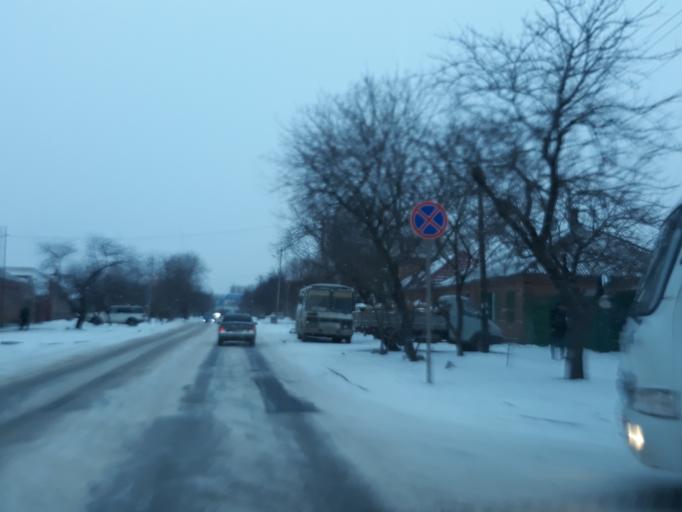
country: RU
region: Rostov
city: Taganrog
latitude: 47.2615
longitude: 38.9298
